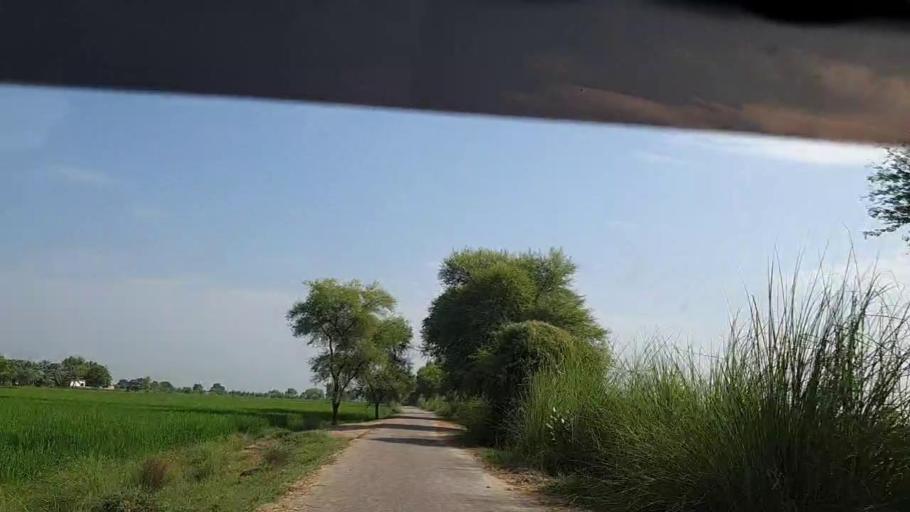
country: PK
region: Sindh
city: Shikarpur
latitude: 28.0959
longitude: 68.6751
